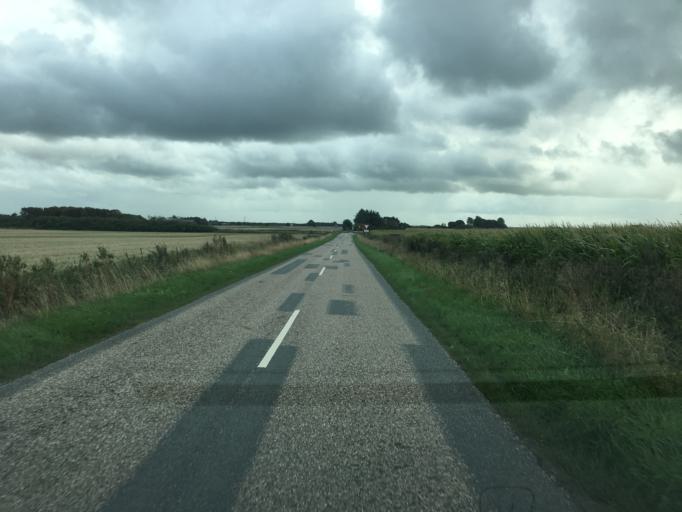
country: DK
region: South Denmark
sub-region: Tonder Kommune
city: Tonder
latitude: 54.9521
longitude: 8.8241
